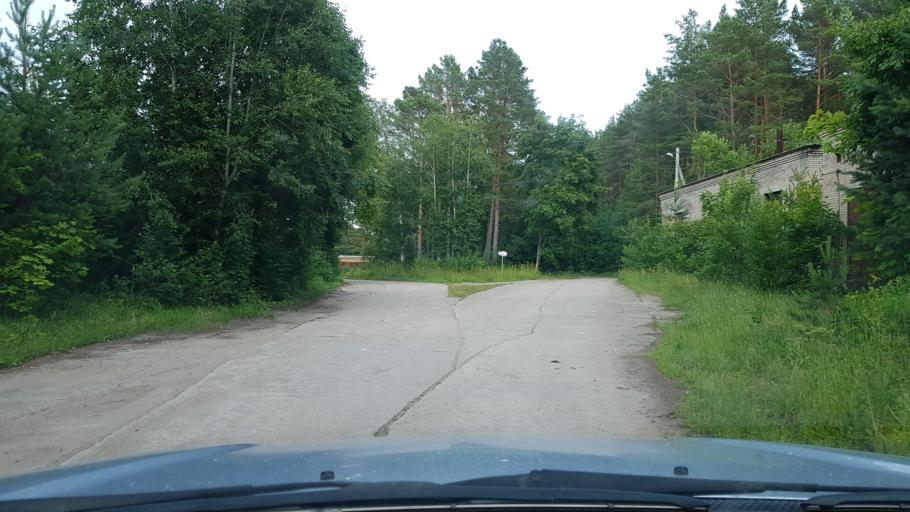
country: EE
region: Ida-Virumaa
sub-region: Narva-Joesuu linn
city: Narva-Joesuu
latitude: 59.4587
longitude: 28.0610
